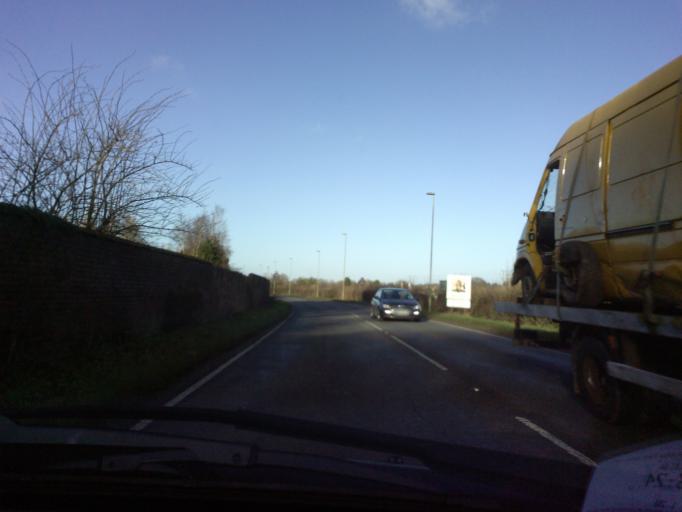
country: GB
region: England
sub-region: Hampshire
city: Romsey
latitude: 50.9844
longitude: -1.4870
